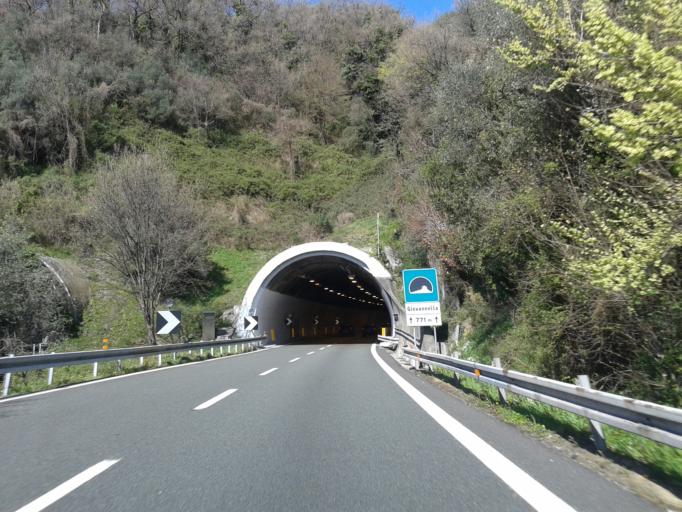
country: IT
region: Liguria
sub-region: Provincia di Genova
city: Moneglia
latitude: 44.2552
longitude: 9.4890
